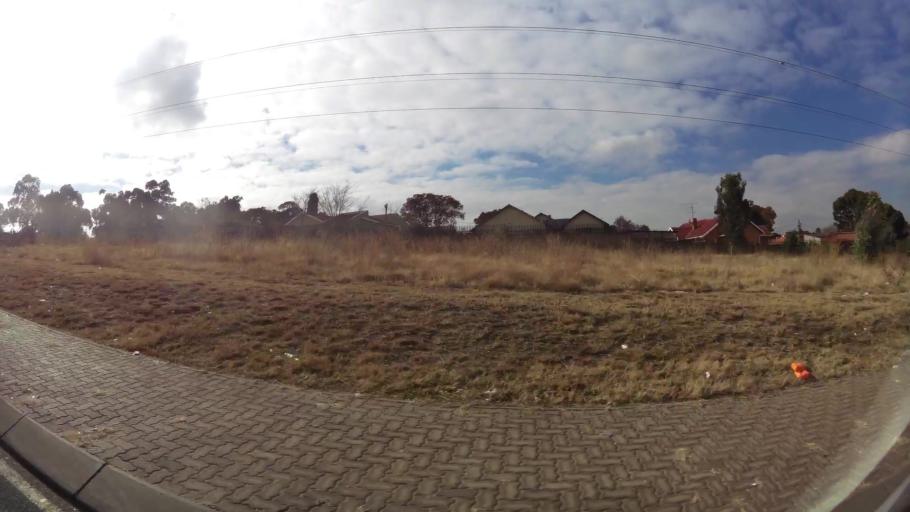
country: ZA
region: Gauteng
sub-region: City of Johannesburg Metropolitan Municipality
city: Roodepoort
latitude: -26.1976
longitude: 27.9118
